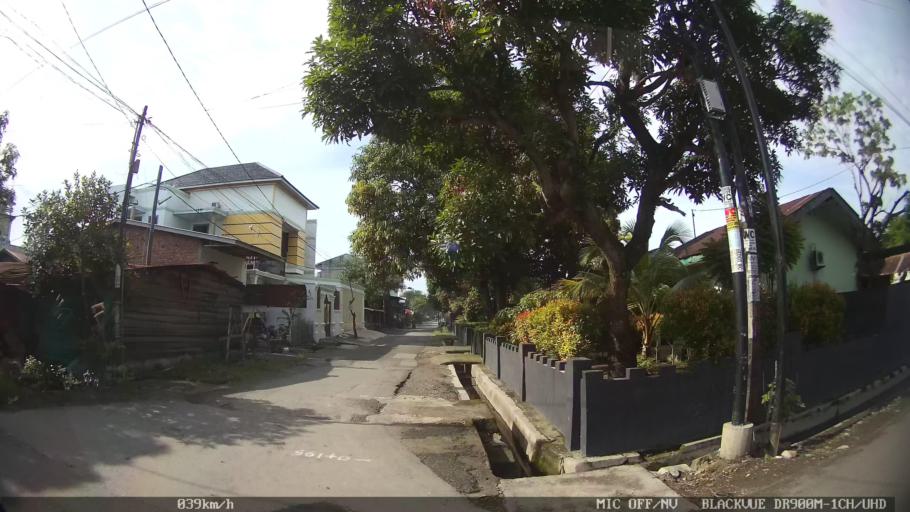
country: ID
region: North Sumatra
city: Medan
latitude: 3.6117
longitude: 98.6496
